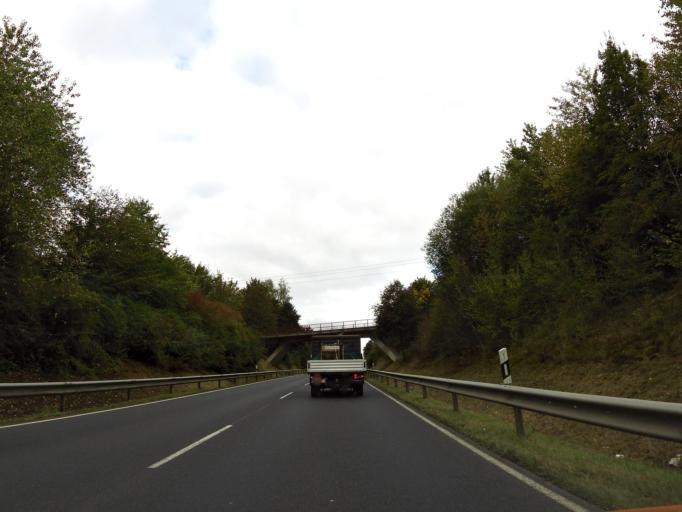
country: DE
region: Lower Saxony
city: Einbeck
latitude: 51.8108
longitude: 9.8426
